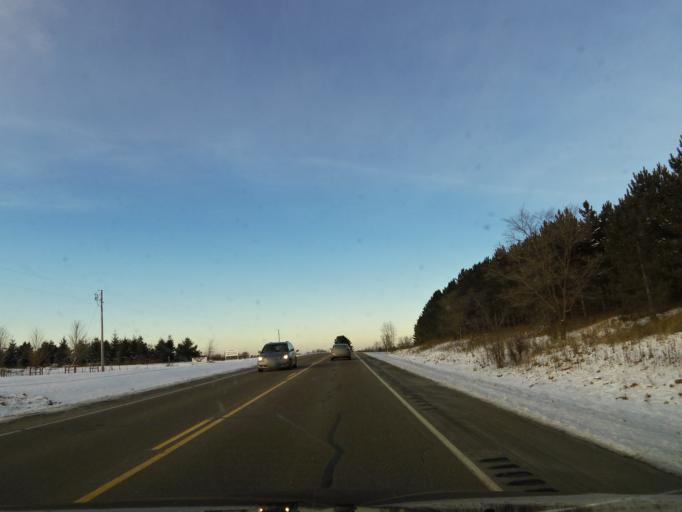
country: US
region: Minnesota
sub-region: Chisago County
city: Shafer
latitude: 45.3649
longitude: -92.7128
